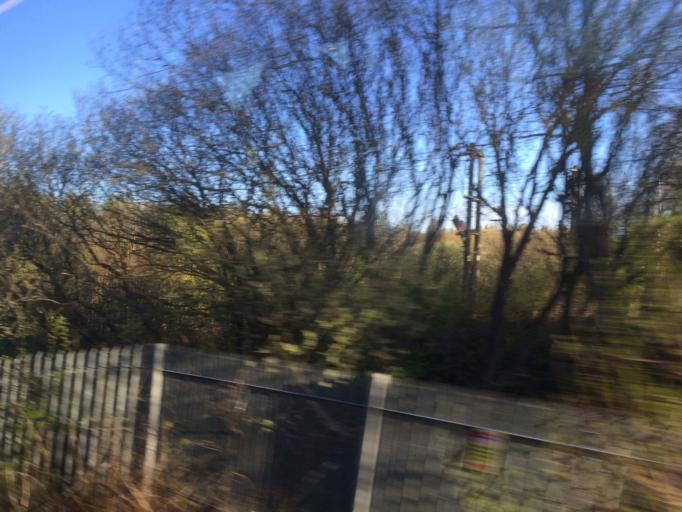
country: GB
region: Scotland
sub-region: South Lanarkshire
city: Rutherglen
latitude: 55.8308
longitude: -4.1784
